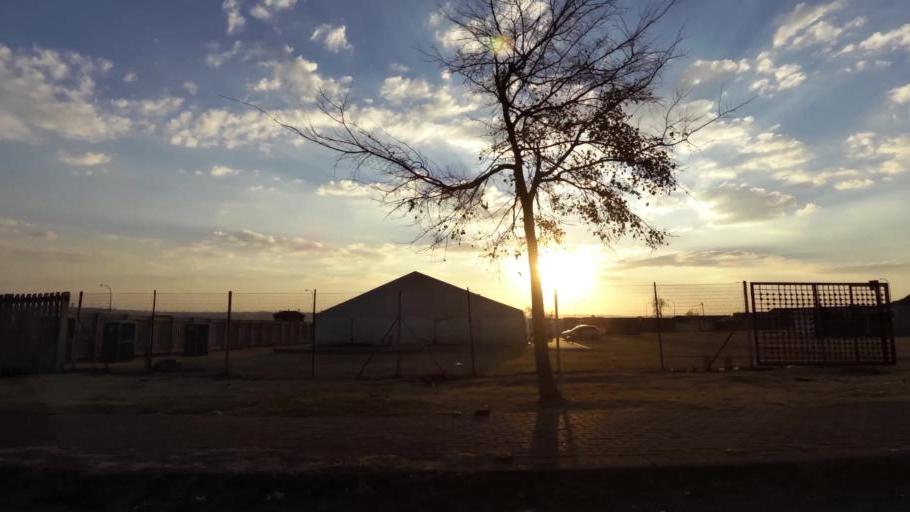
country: ZA
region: Gauteng
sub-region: City of Johannesburg Metropolitan Municipality
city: Soweto
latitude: -26.2307
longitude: 27.8963
